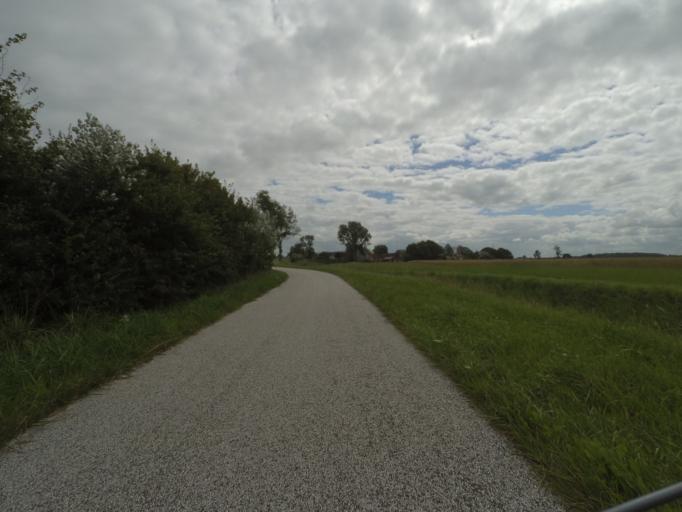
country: NL
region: Friesland
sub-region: Gemeente Kollumerland en Nieuwkruisland
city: Kollum
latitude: 53.3205
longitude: 6.1555
